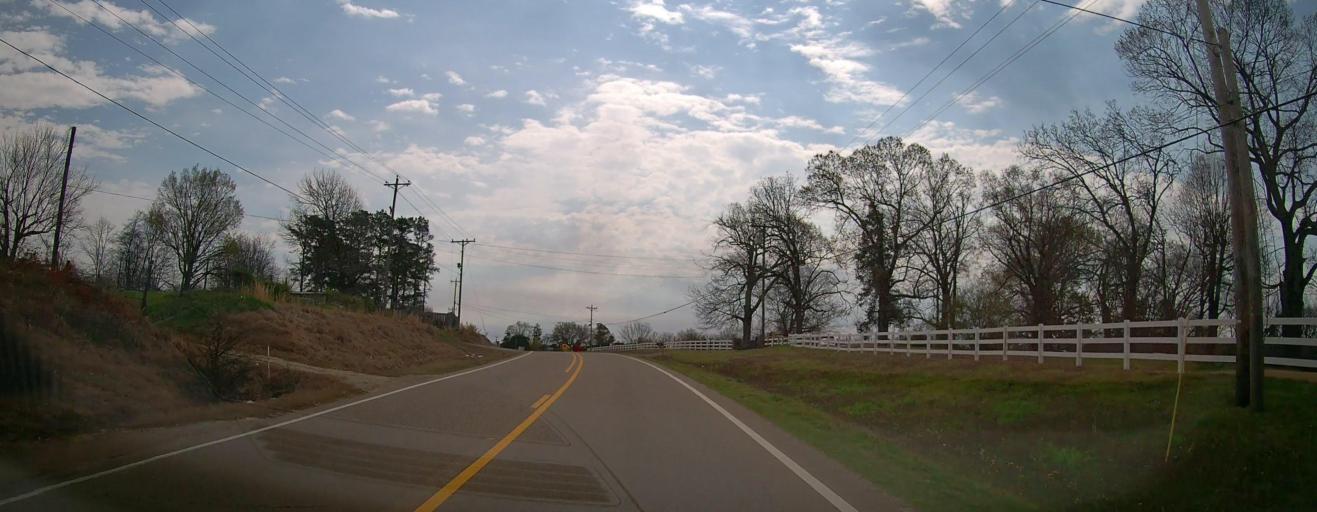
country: US
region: Mississippi
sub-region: De Soto County
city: Olive Branch
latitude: 34.9815
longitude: -89.8568
